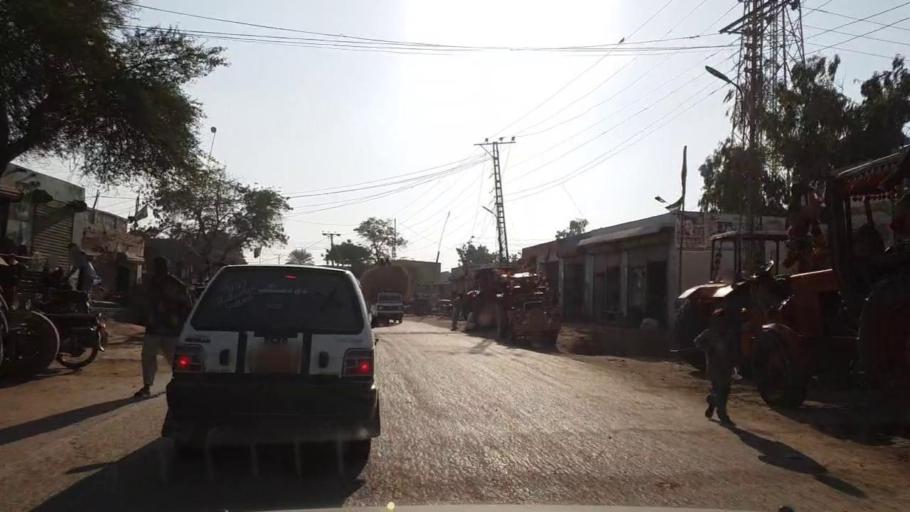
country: PK
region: Sindh
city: Bulri
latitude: 24.8622
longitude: 68.3304
